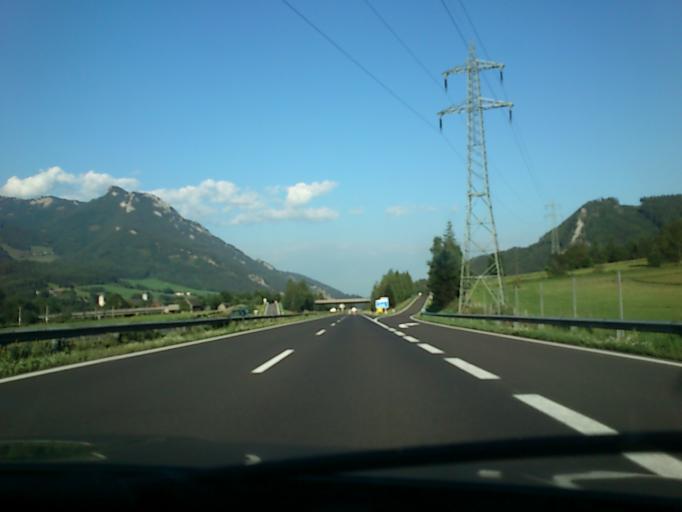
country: AT
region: Styria
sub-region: Politischer Bezirk Leoben
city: Mautern in Steiermark
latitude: 47.3964
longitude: 14.8091
